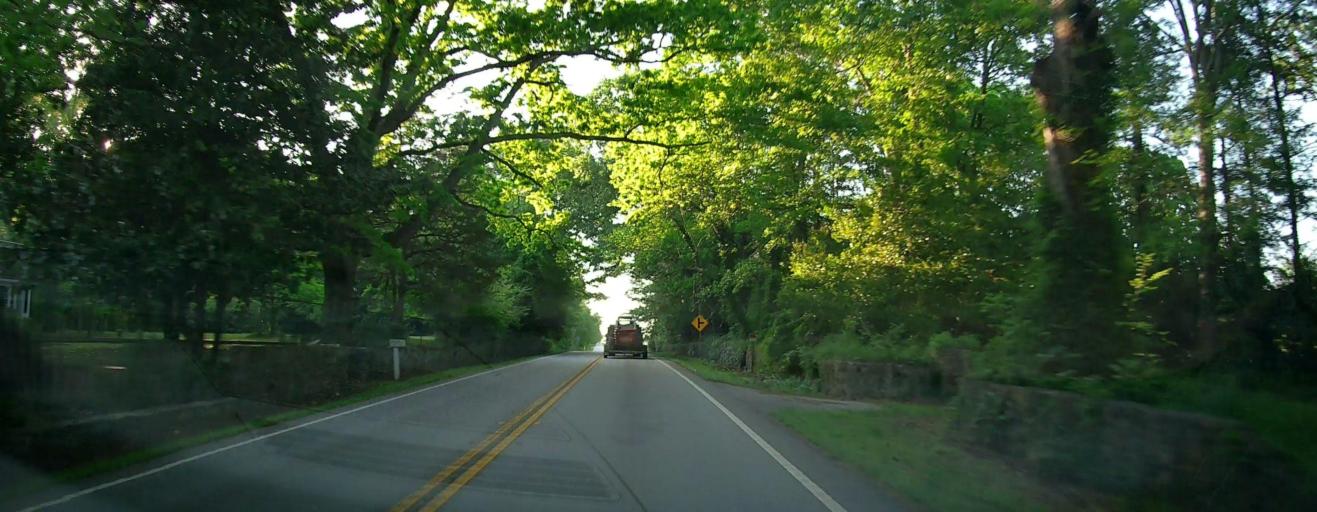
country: US
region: Georgia
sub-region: Walton County
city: Social Circle
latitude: 33.5448
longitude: -83.7294
